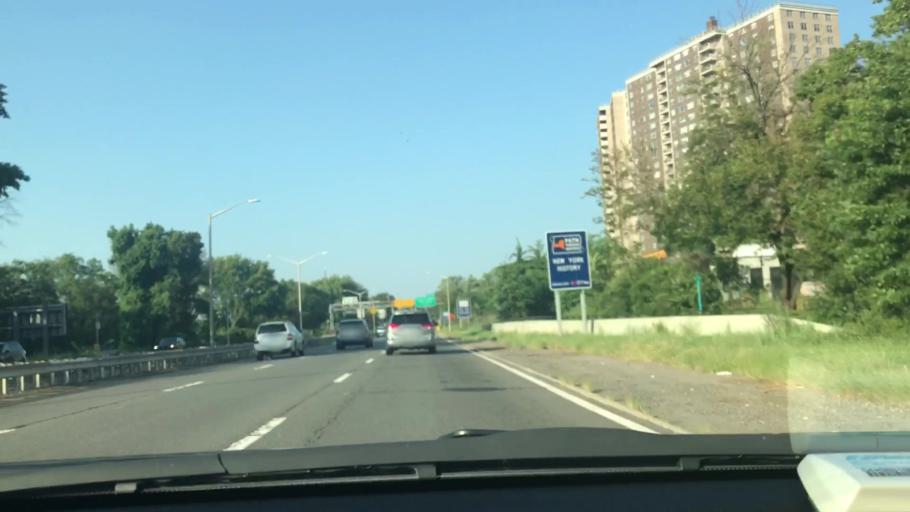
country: US
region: New York
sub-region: Bronx
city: Eastchester
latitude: 40.8636
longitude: -73.8259
